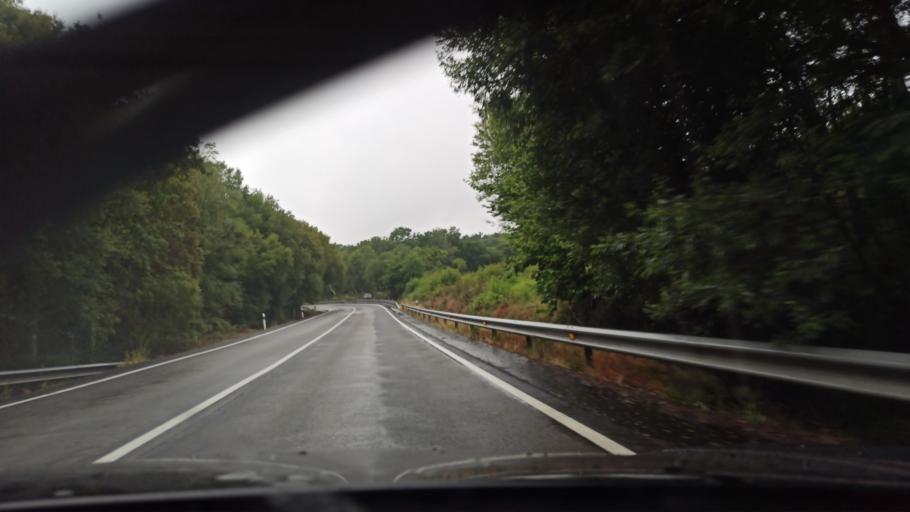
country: ES
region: Galicia
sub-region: Provincia de Lugo
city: Guntin
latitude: 42.8380
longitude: -7.7550
